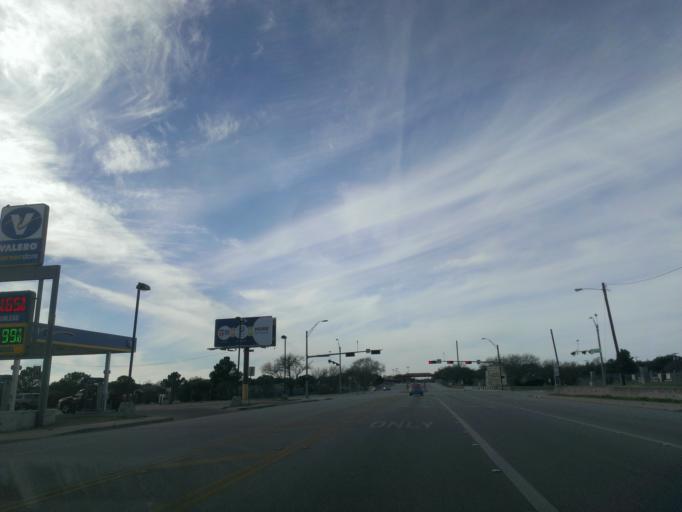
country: US
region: Texas
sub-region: Bell County
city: Killeen
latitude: 31.1294
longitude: -97.7386
